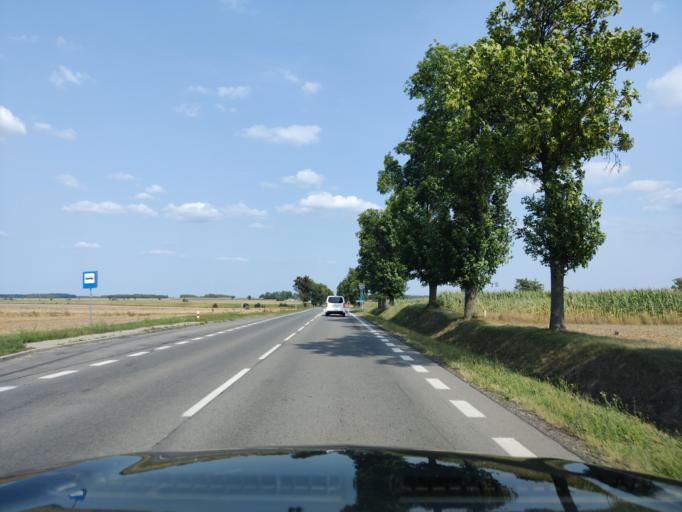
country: PL
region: Masovian Voivodeship
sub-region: Powiat makowski
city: Rzewnie
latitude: 52.8596
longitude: 21.3125
